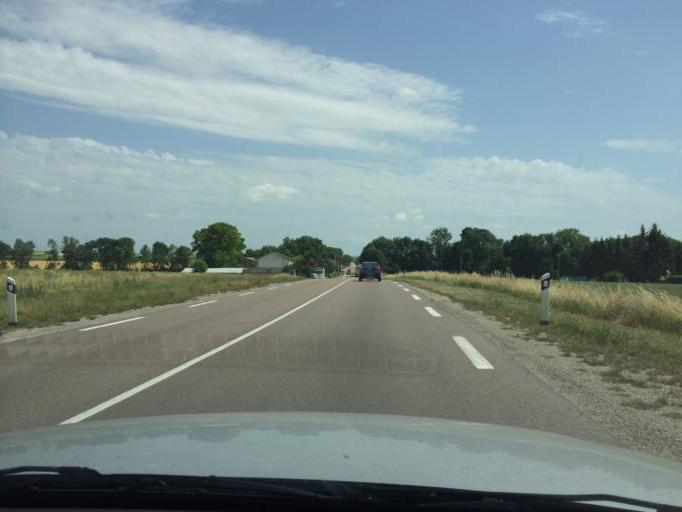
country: FR
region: Champagne-Ardenne
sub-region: Departement de la Marne
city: Sarry
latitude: 48.9085
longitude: 4.4325
